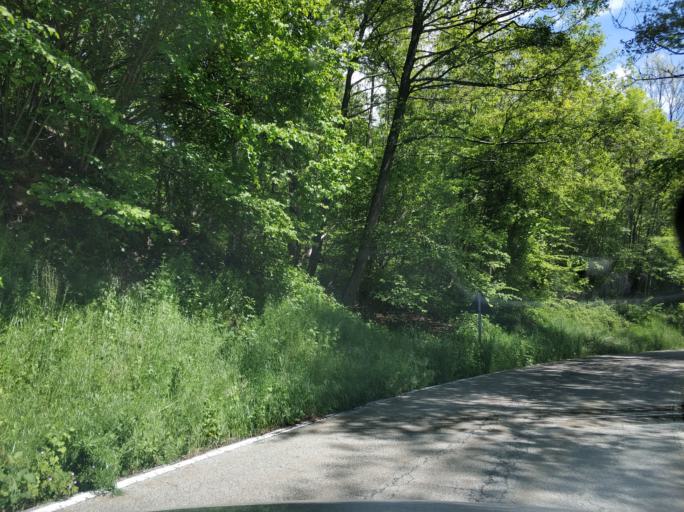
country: IT
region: Piedmont
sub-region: Provincia di Torino
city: Coassolo
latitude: 45.3093
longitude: 7.4686
